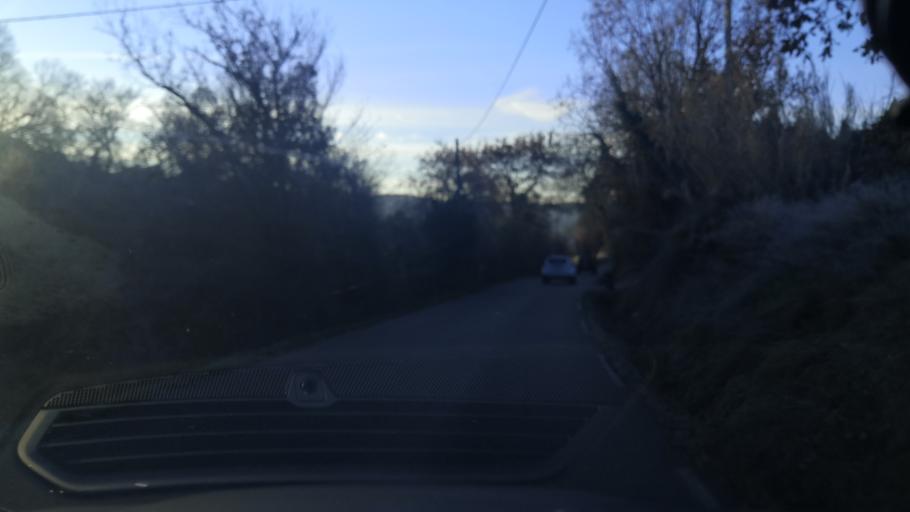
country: FR
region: Provence-Alpes-Cote d'Azur
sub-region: Departement des Bouches-du-Rhone
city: Aix-en-Provence
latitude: 43.5138
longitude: 5.4092
